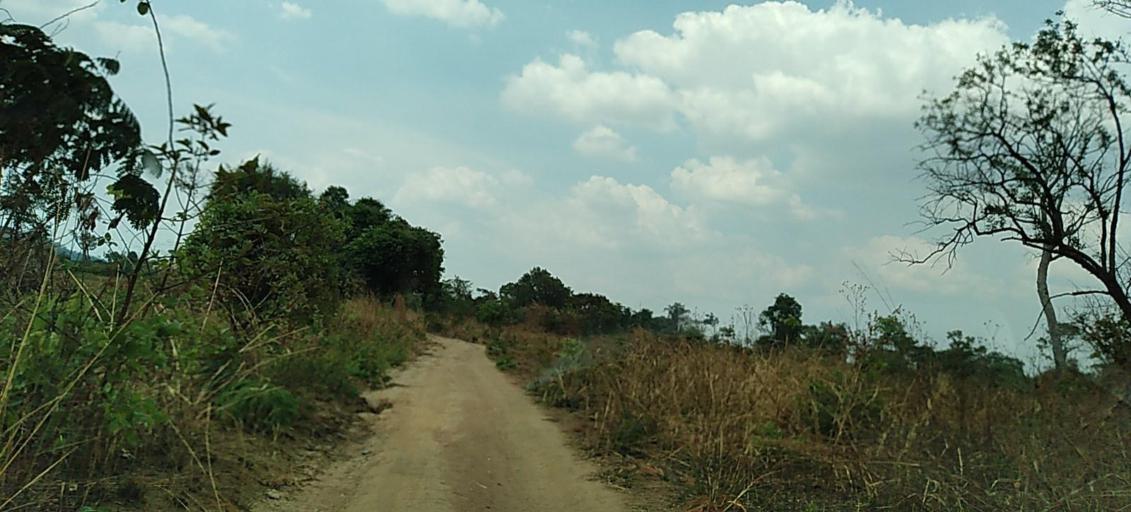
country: ZM
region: Copperbelt
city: Chililabombwe
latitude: -12.3271
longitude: 27.7483
